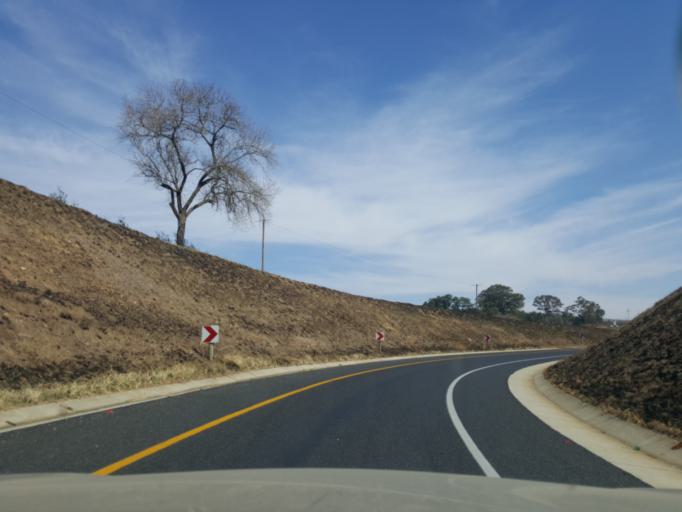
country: ZA
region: Mpumalanga
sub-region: Nkangala District Municipality
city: Belfast
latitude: -25.6124
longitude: 30.2794
